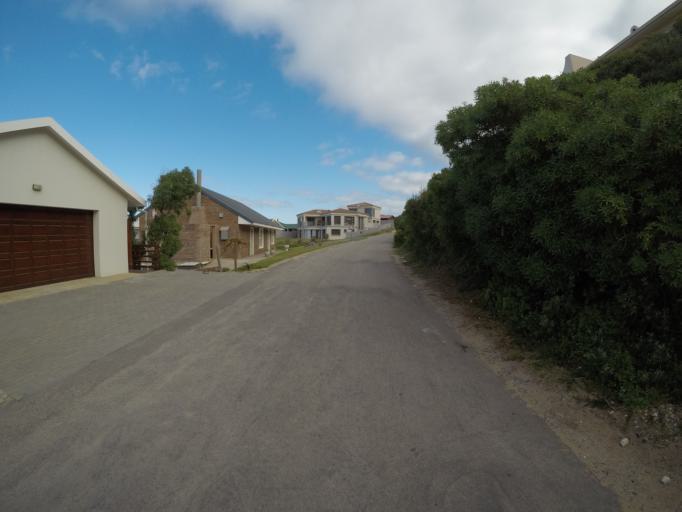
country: ZA
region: Western Cape
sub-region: Eden District Municipality
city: Riversdale
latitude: -34.4302
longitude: 21.3327
